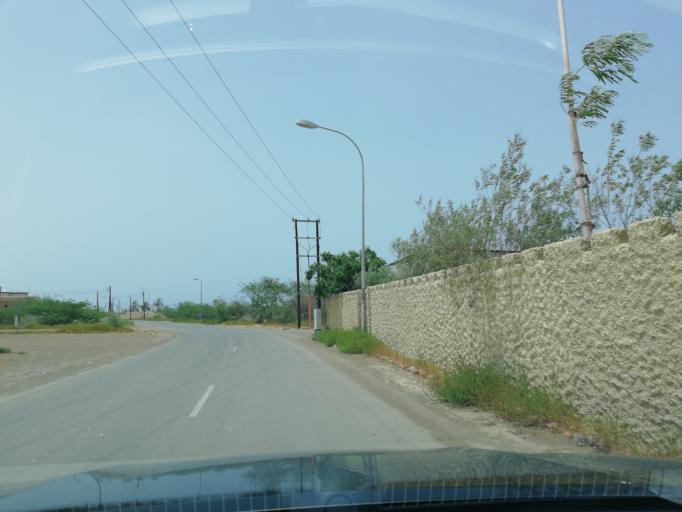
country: OM
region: Al Batinah
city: Al Liwa'
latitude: 24.6092
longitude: 56.5381
